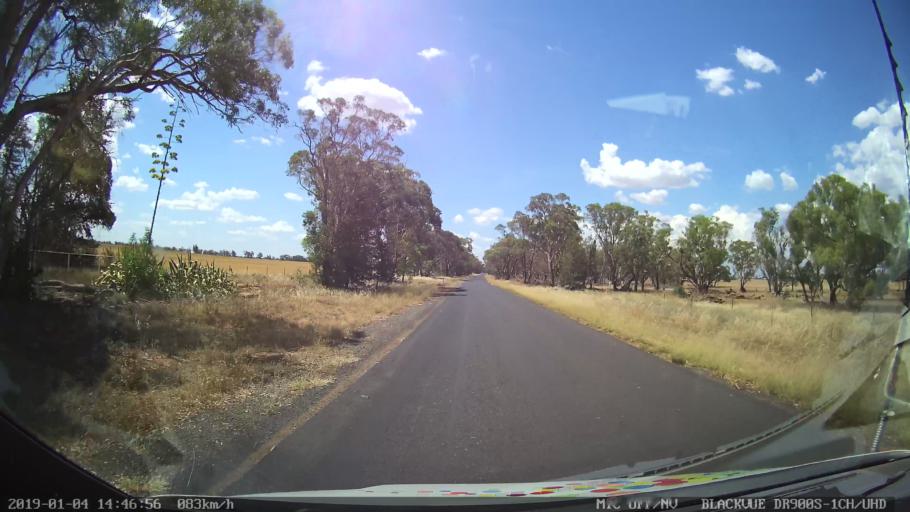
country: AU
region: New South Wales
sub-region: Dubbo Municipality
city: Dubbo
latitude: -32.0754
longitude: 148.6592
